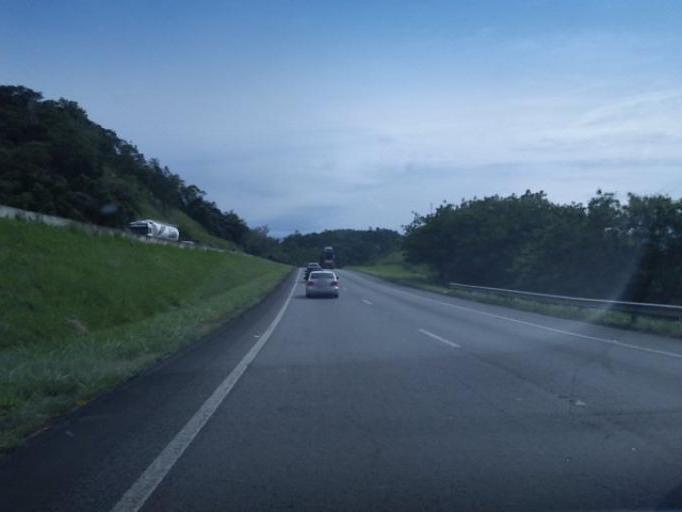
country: BR
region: Sao Paulo
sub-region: Cajati
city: Cajati
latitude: -24.7472
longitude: -48.1491
